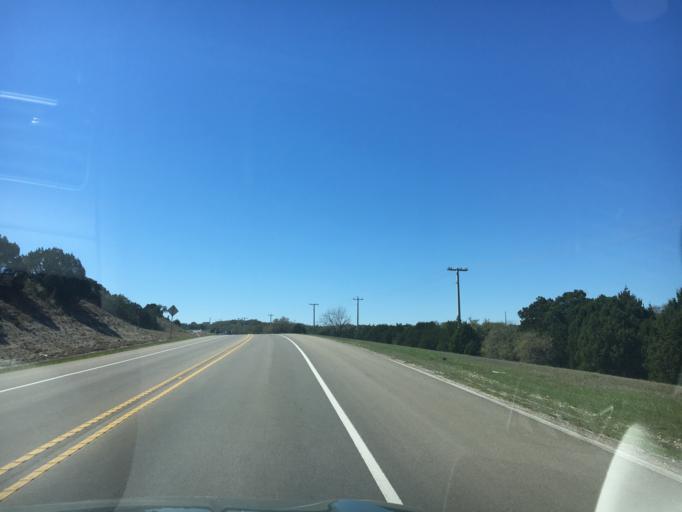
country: US
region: Texas
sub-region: Travis County
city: The Hills
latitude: 30.2873
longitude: -98.0544
